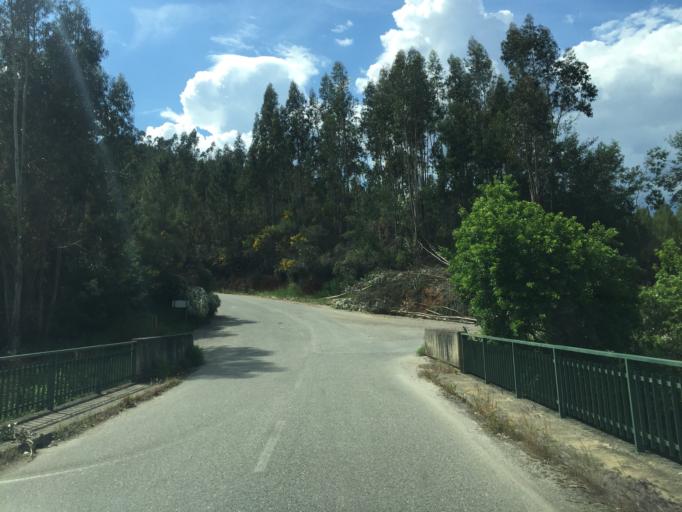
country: PT
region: Coimbra
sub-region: Pampilhosa da Serra
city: Pampilhosa da Serra
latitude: 40.0556
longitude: -7.8073
